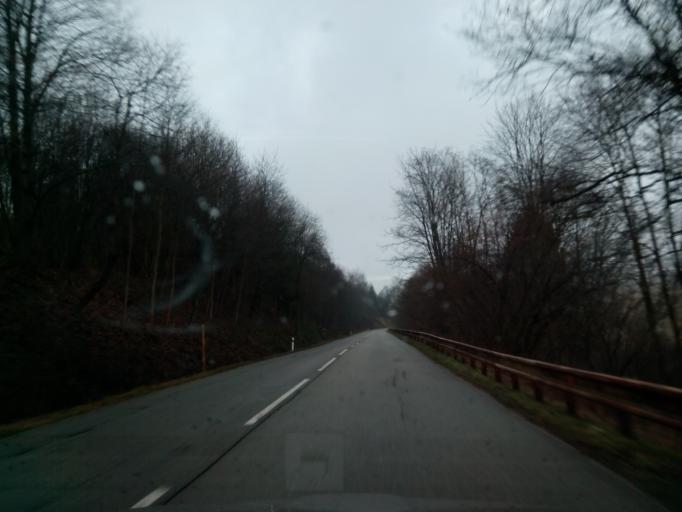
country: SK
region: Kosicky
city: Gelnica
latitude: 48.8464
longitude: 21.0349
